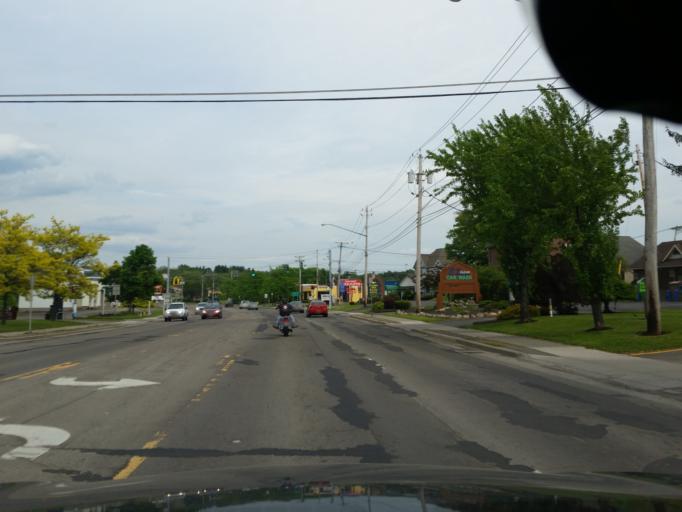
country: US
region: New York
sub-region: Chautauqua County
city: Celoron
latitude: 42.0981
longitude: -79.2965
